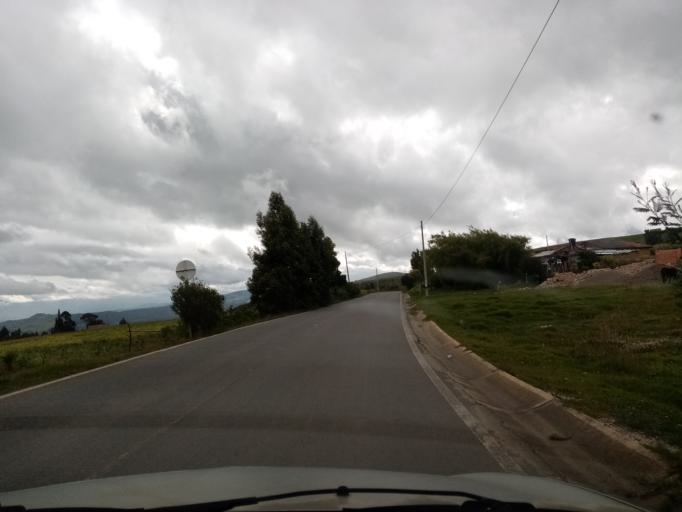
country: CO
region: Boyaca
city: Siachoque
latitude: 5.5650
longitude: -73.2805
